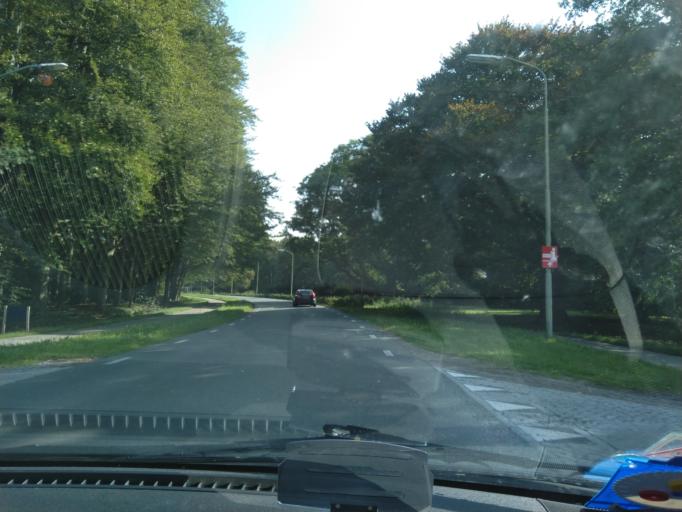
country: NL
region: Groningen
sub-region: Gemeente Haren
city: Haren
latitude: 53.1638
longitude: 6.5555
